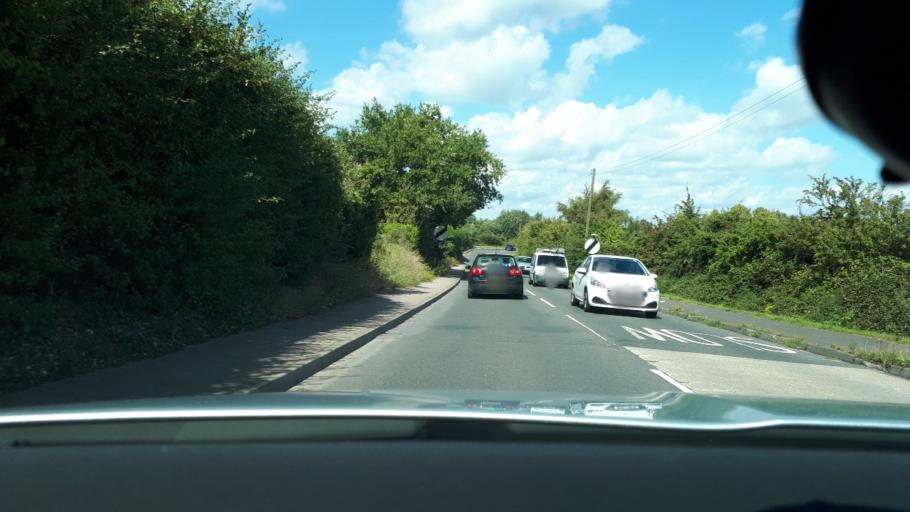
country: GB
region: England
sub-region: Kent
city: Swanley
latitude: 51.4083
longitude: 0.1599
